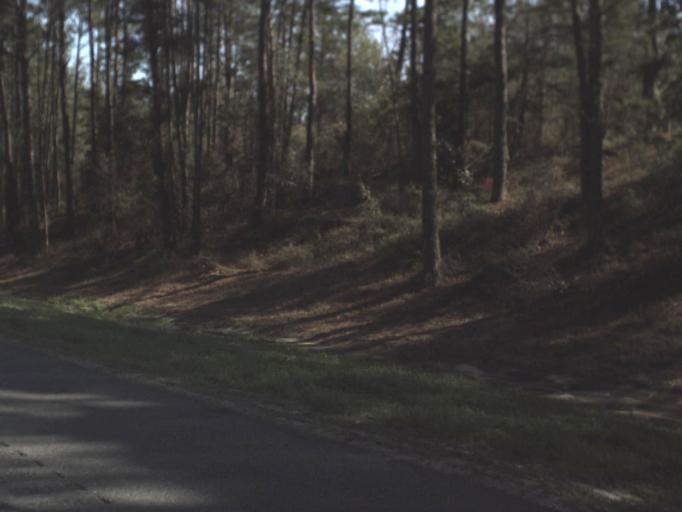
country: US
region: Florida
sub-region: Gadsden County
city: Midway
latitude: 30.5209
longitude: -84.4902
